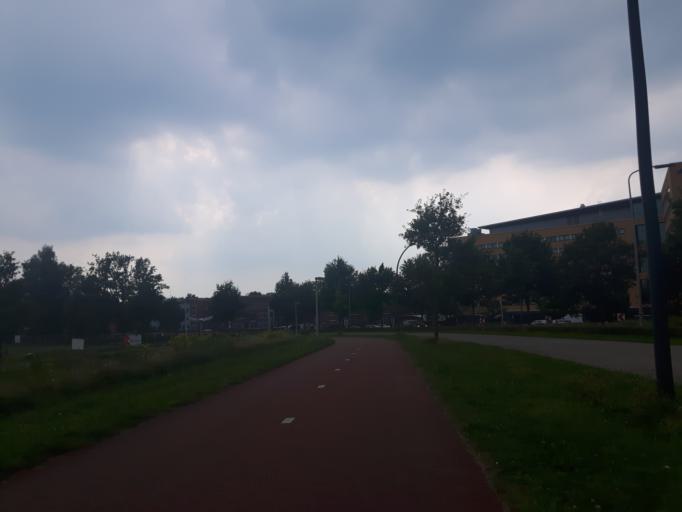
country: NL
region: Overijssel
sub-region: Gemeente Hengelo
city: Hengelo
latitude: 52.2876
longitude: 6.7831
